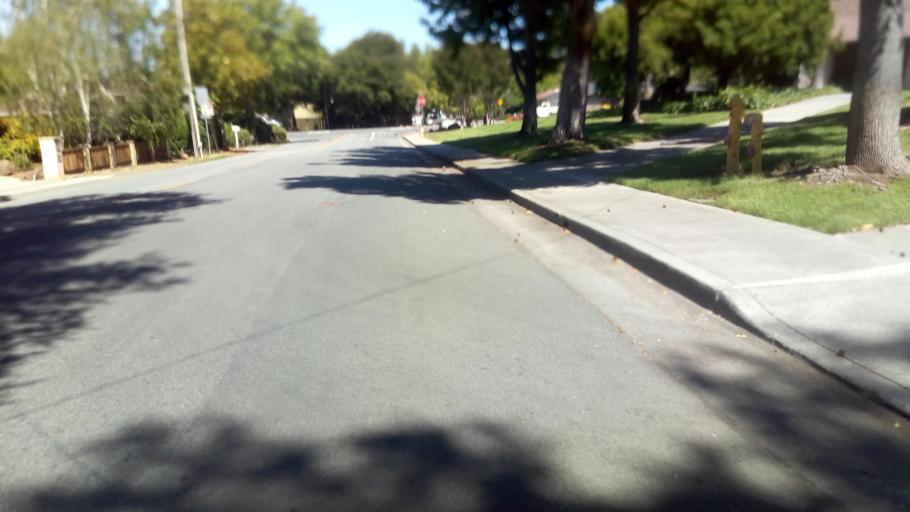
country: US
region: California
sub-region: Santa Clara County
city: Loyola
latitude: 37.3595
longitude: -122.0789
